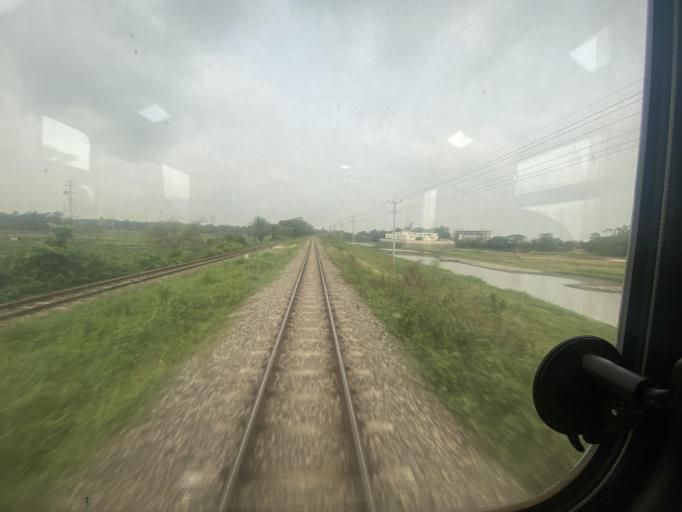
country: BD
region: Dhaka
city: Tungi
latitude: 23.9334
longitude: 90.4997
